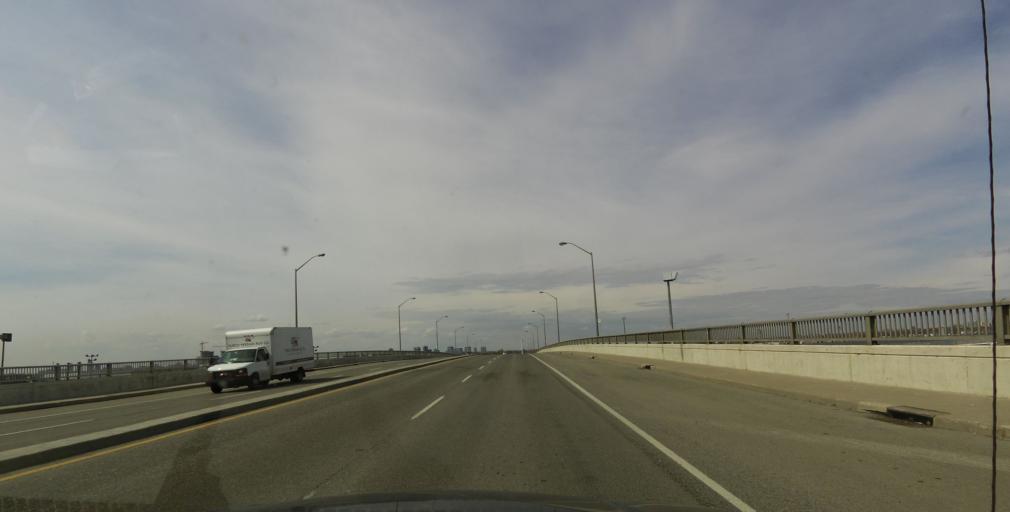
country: CA
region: Ontario
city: Etobicoke
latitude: 43.6096
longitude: -79.5072
